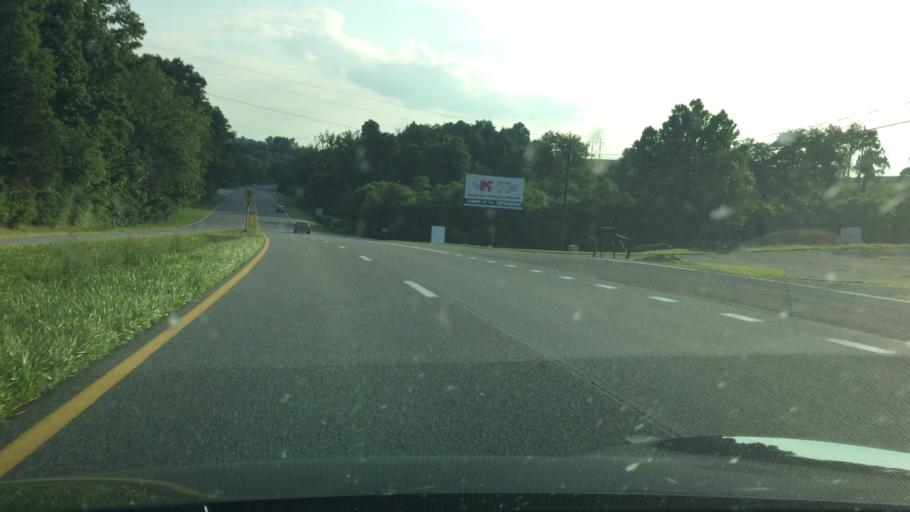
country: US
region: Virginia
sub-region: Pulaski County
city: Fairlawn
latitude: 37.1373
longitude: -80.6130
